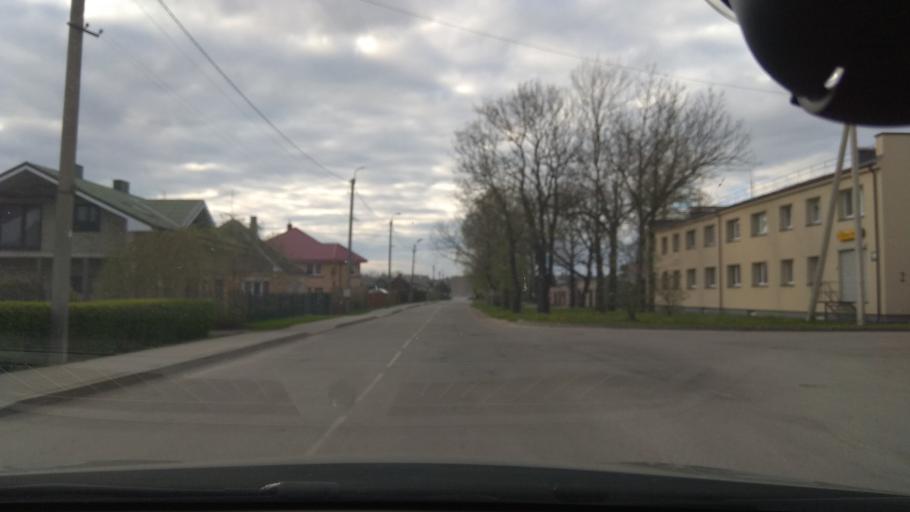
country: LT
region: Siauliu apskritis
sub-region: Joniskis
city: Joniskis
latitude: 56.2449
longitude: 23.6143
